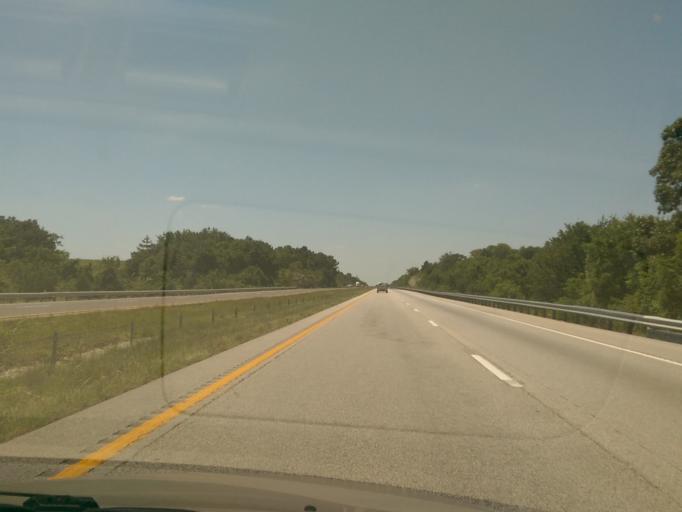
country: US
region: Missouri
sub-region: Cooper County
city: Boonville
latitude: 38.9338
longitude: -92.9555
